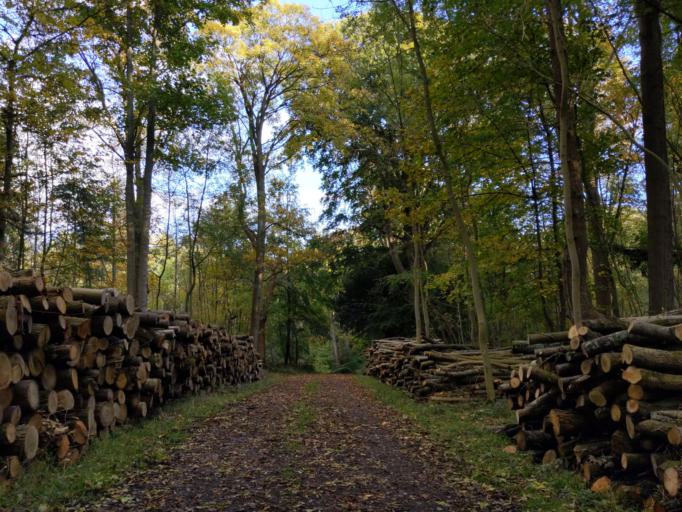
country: GB
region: England
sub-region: Oxfordshire
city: Oxford
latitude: 51.7202
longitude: -1.2604
